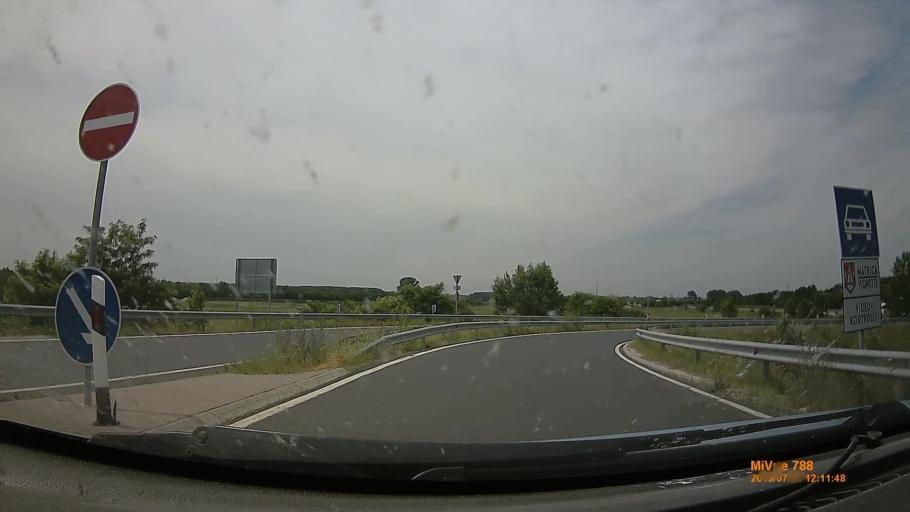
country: HU
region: Pest
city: Vecses
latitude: 47.3757
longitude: 19.2638
